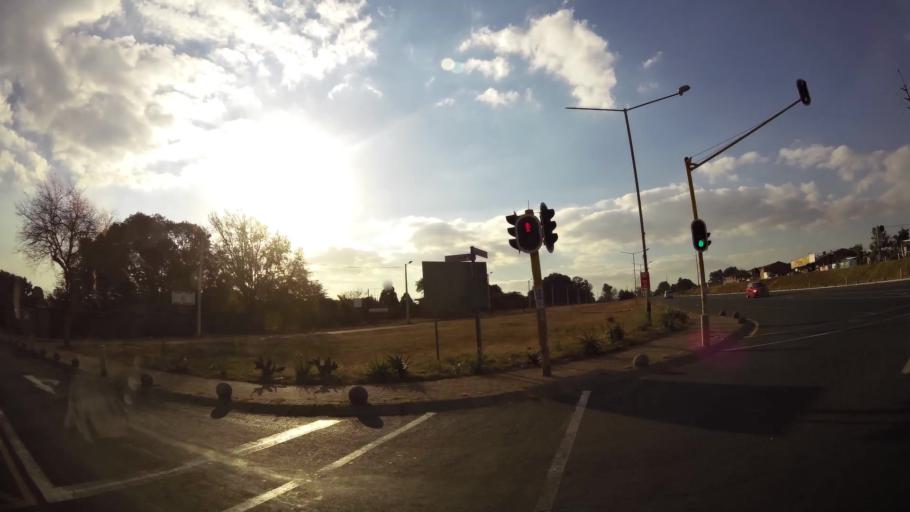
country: ZA
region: Gauteng
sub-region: West Rand District Municipality
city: Krugersdorp
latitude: -26.0892
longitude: 27.7601
